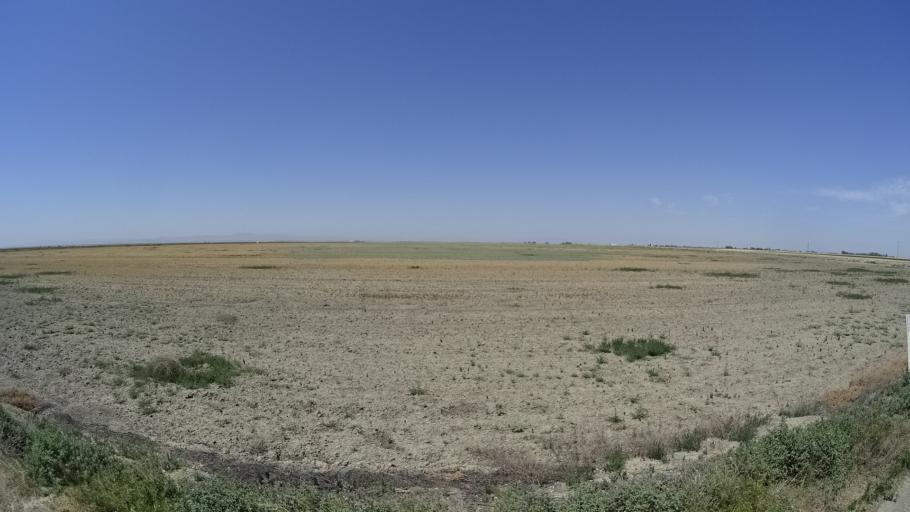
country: US
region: California
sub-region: Kings County
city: Stratford
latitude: 36.1408
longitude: -119.7444
